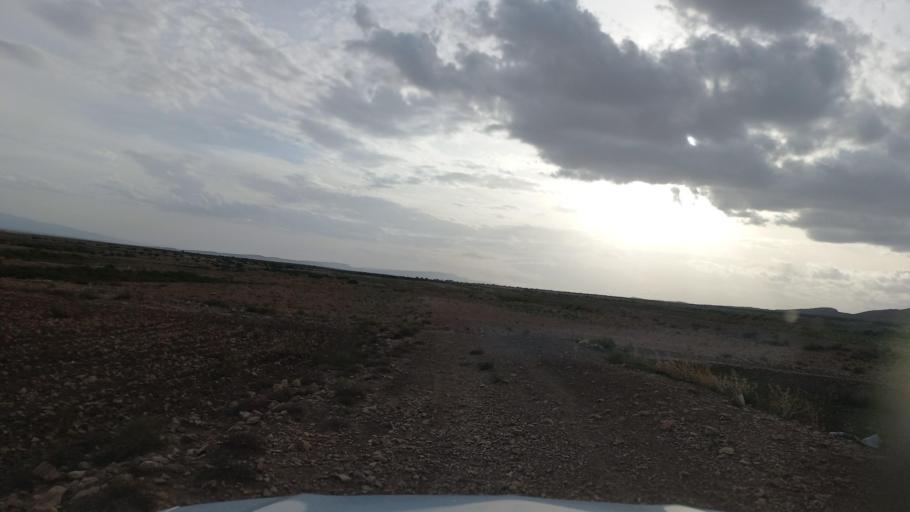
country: TN
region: Al Qasrayn
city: Sbiba
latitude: 35.4478
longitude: 9.0627
